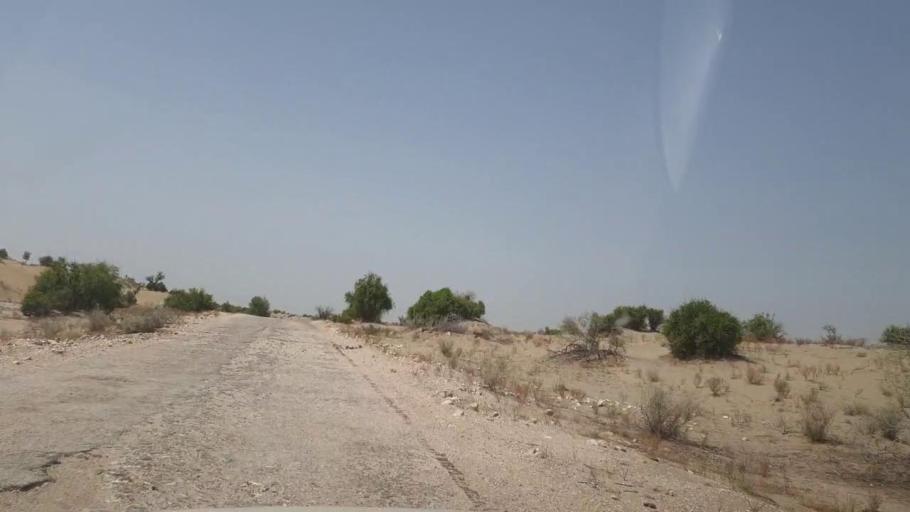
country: PK
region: Sindh
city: Khanpur
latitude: 27.3673
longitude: 69.3170
